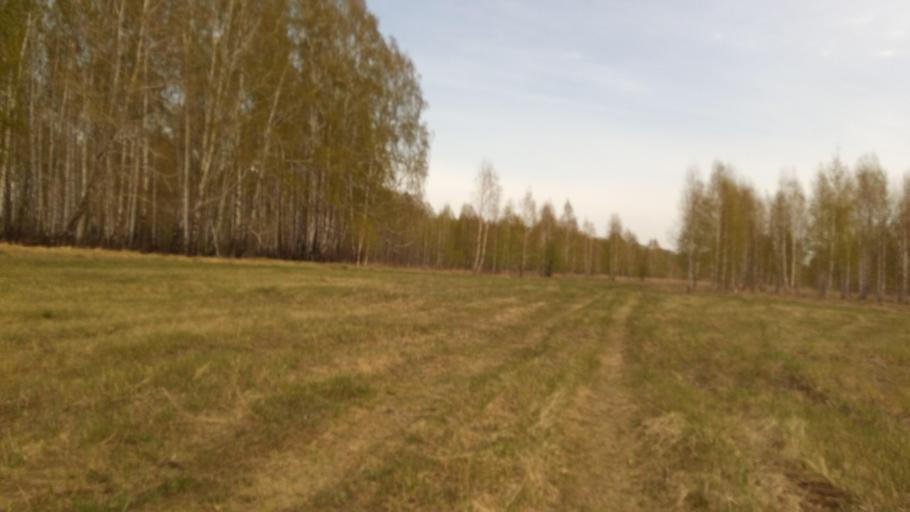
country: RU
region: Chelyabinsk
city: Timiryazevskiy
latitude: 55.0017
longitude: 60.8495
